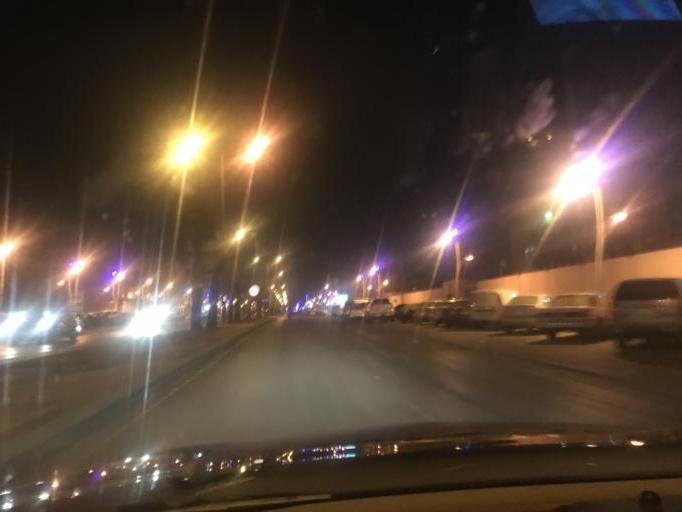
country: SA
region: Ar Riyad
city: Riyadh
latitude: 24.7609
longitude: 46.7989
